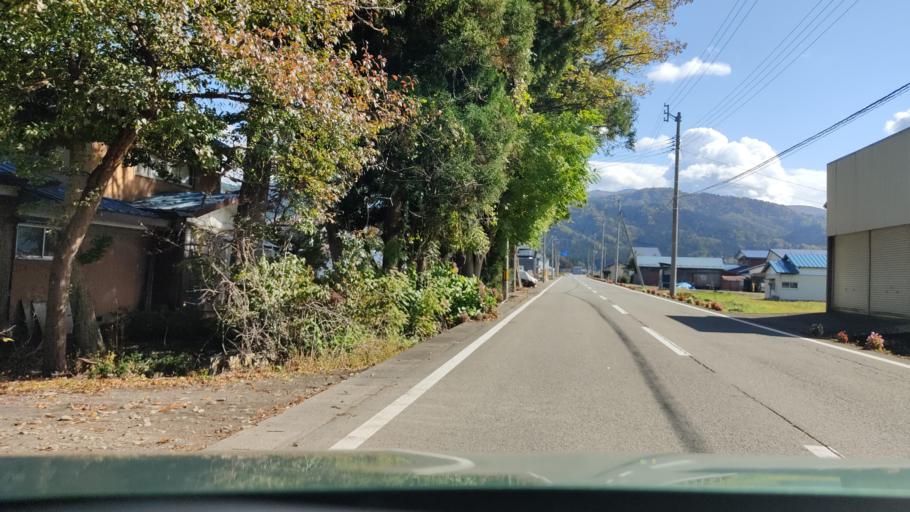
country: JP
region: Akita
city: Yokotemachi
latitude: 39.4071
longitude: 140.5754
